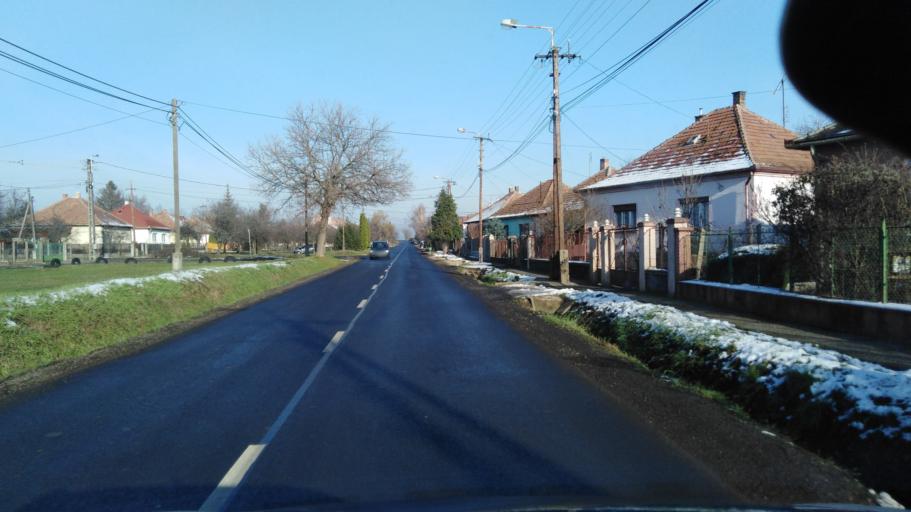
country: HU
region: Nograd
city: Paszto
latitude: 47.9271
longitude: 19.7030
